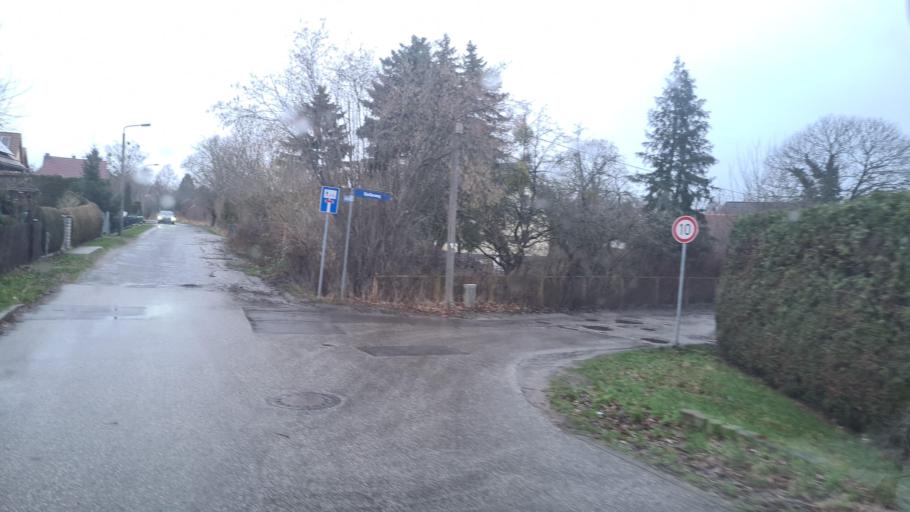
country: DE
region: Brandenburg
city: Teltow
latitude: 52.3993
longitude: 13.2853
